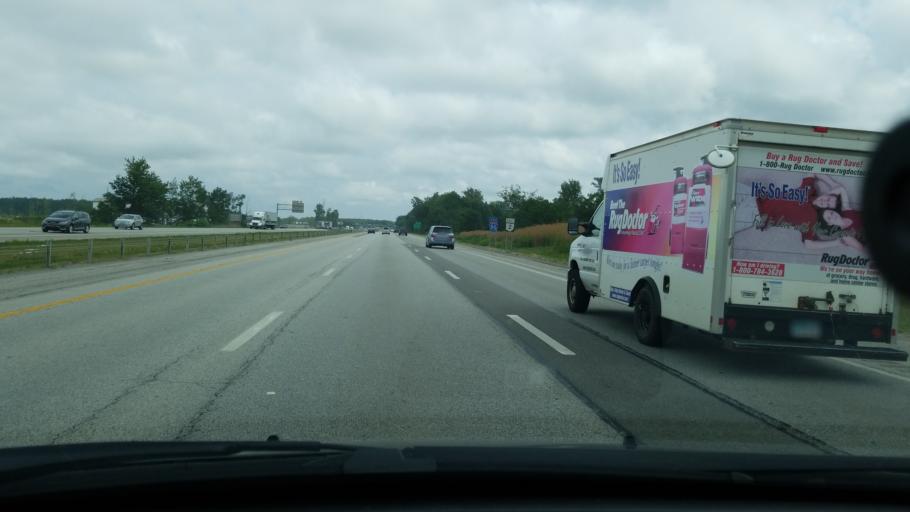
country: US
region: Ohio
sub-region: Lorain County
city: Avon Center
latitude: 41.4643
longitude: -82.0123
